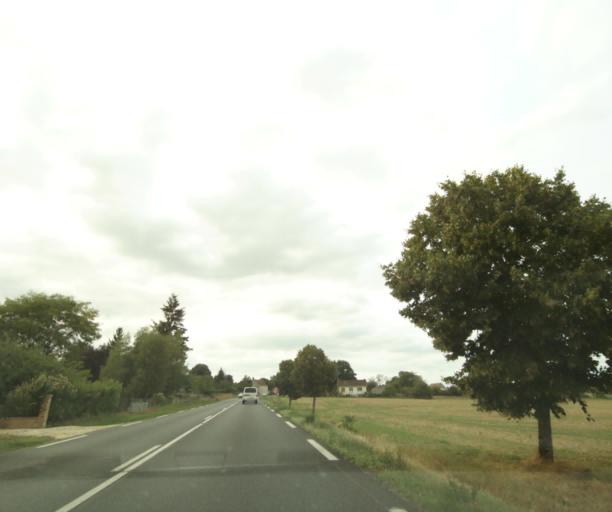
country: FR
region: Centre
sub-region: Departement d'Indre-et-Loire
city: Perrusson
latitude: 47.0845
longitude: 1.0289
